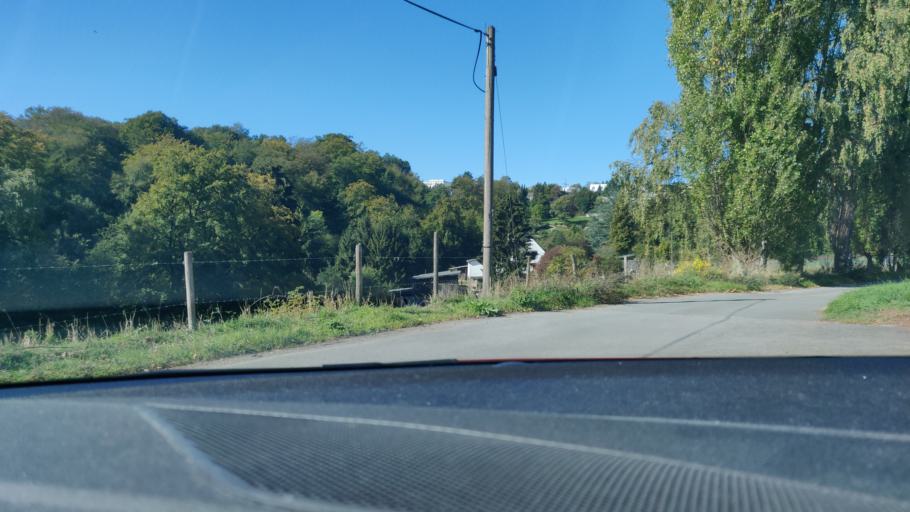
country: DE
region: North Rhine-Westphalia
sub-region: Regierungsbezirk Dusseldorf
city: Velbert
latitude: 51.3393
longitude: 7.0734
